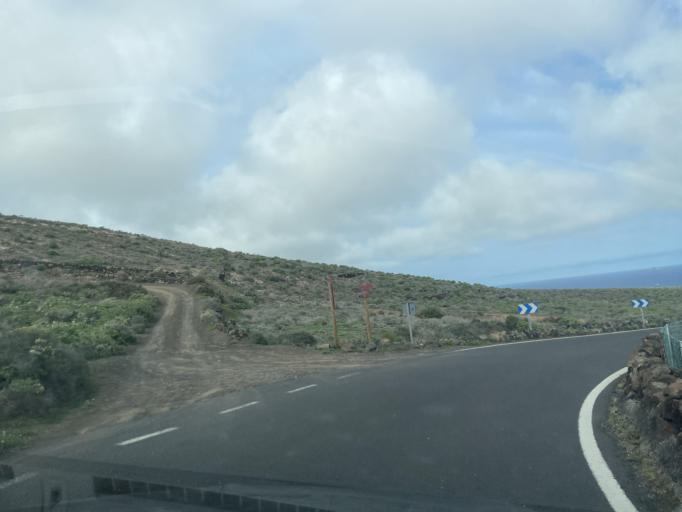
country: ES
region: Canary Islands
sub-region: Provincia de Las Palmas
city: Haria
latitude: 29.1970
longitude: -13.4587
